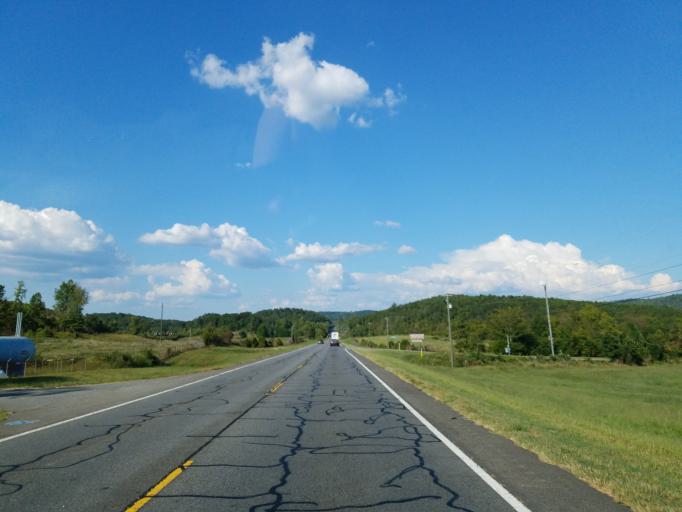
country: US
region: Georgia
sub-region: Bartow County
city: Rydal
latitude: 34.3621
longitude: -84.7162
